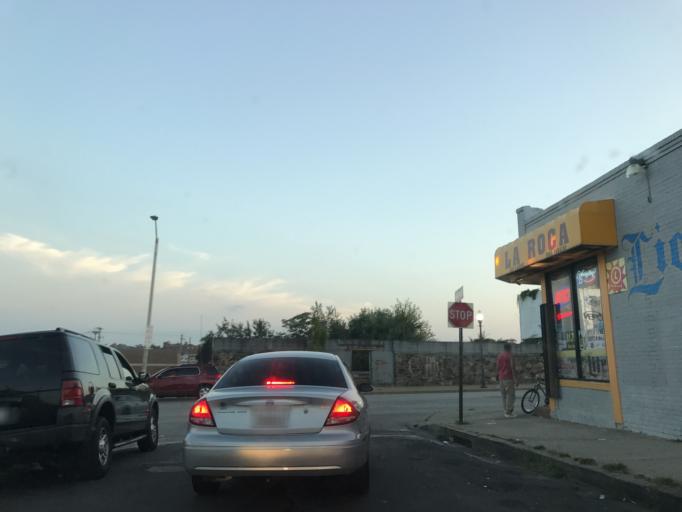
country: US
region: Maryland
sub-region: City of Baltimore
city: Baltimore
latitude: 39.2960
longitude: -76.5721
